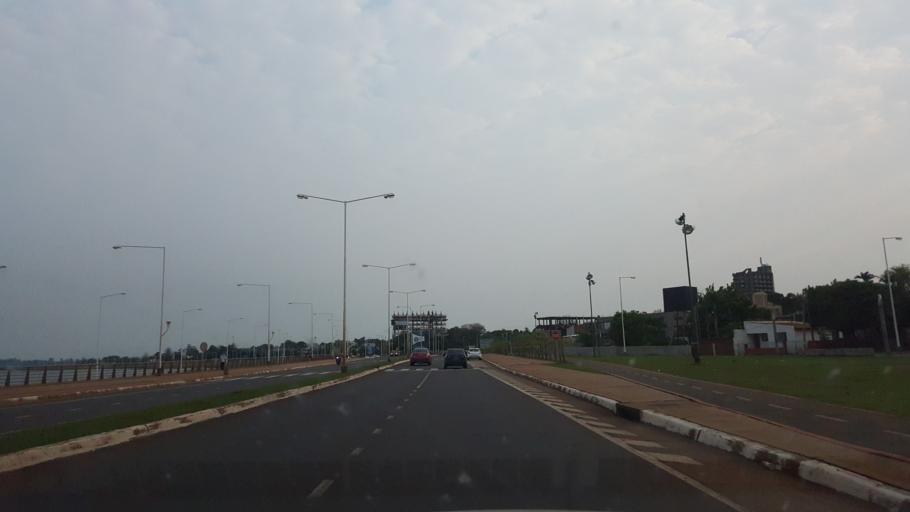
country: AR
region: Misiones
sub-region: Departamento de Capital
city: Posadas
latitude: -27.3897
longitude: -55.8905
